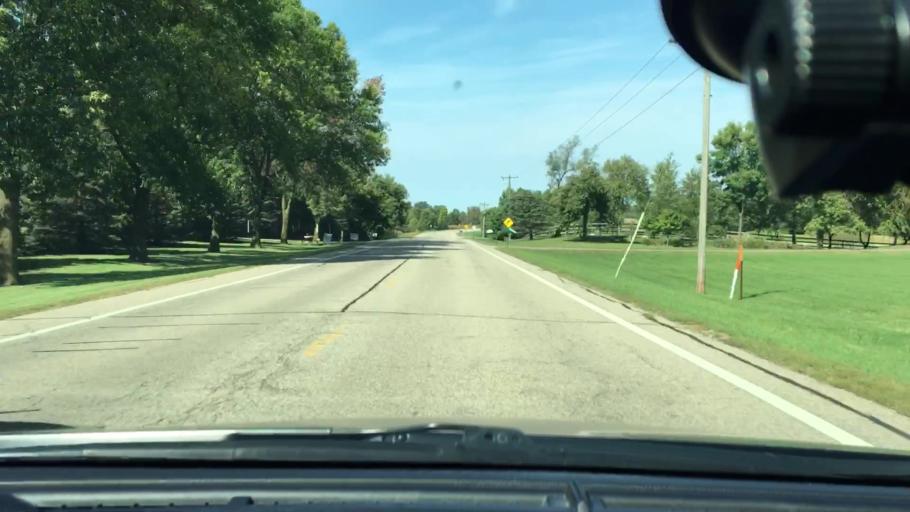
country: US
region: Minnesota
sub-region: Hennepin County
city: Corcoran
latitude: 45.1034
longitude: -93.5601
